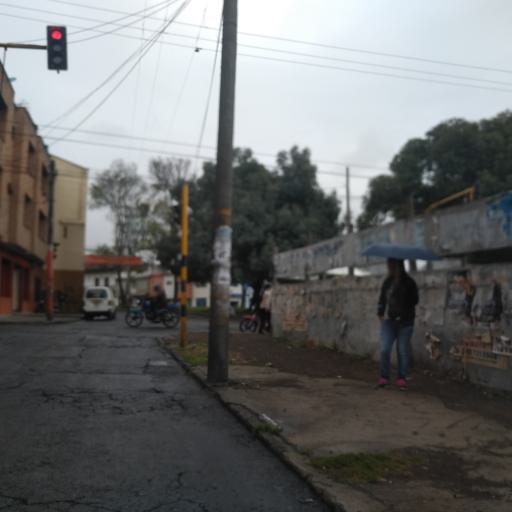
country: CO
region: Narino
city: Pasto
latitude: 1.2148
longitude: -77.2837
